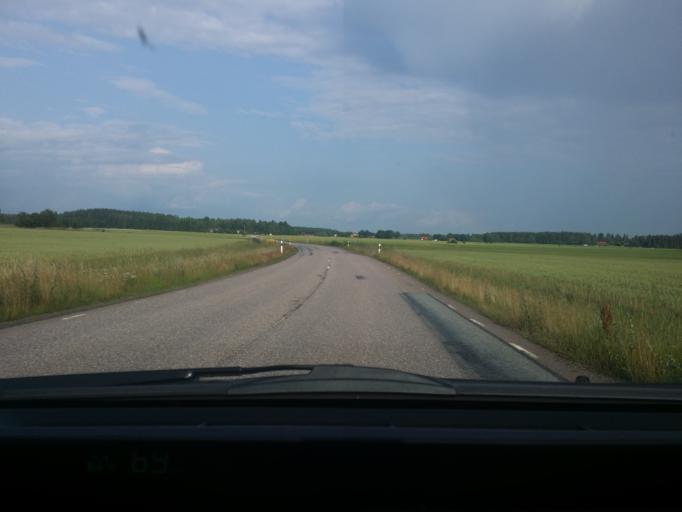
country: SE
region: Vaestmanland
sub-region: Hallstahammars Kommun
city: Kolback
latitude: 59.5627
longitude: 16.2913
